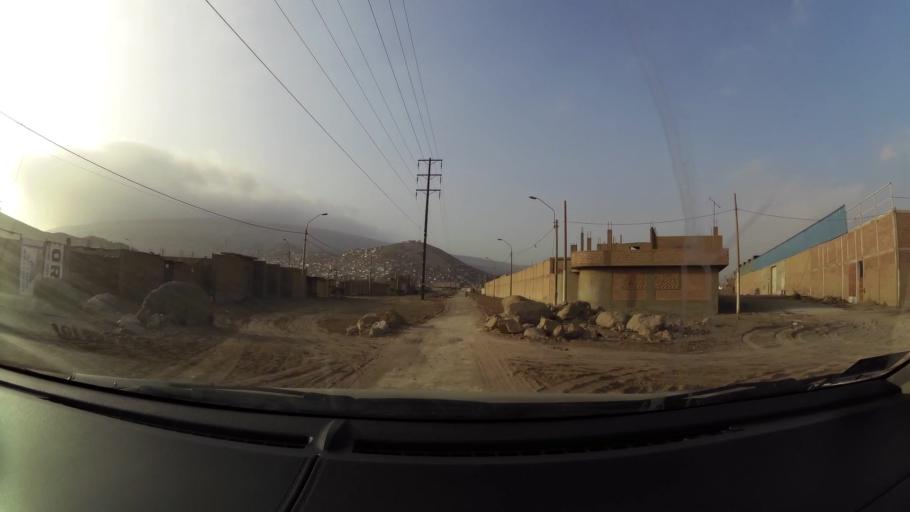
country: PE
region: Lima
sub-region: Lima
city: Santa Rosa
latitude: -11.7504
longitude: -77.1503
